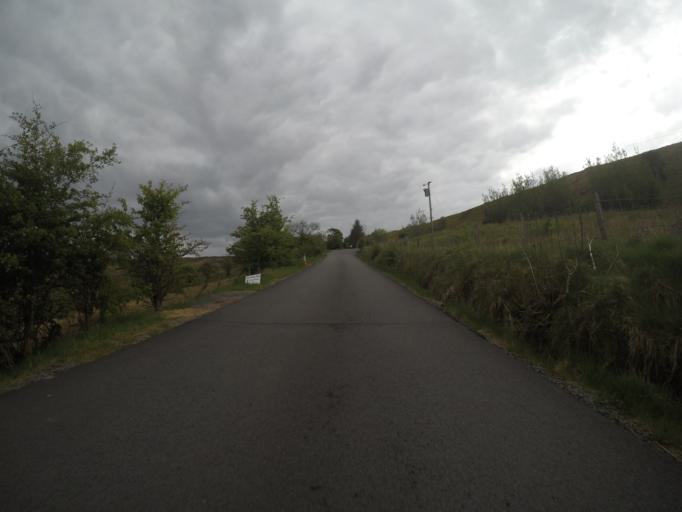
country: GB
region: Scotland
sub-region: Highland
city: Isle of Skye
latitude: 57.3009
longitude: -6.3578
